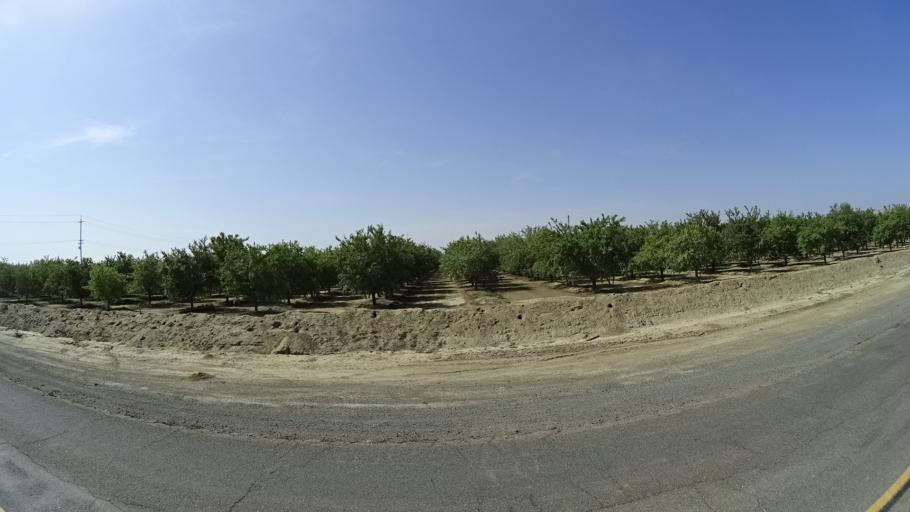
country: US
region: California
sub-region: Kings County
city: Kettleman City
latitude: 36.0364
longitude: -119.9603
